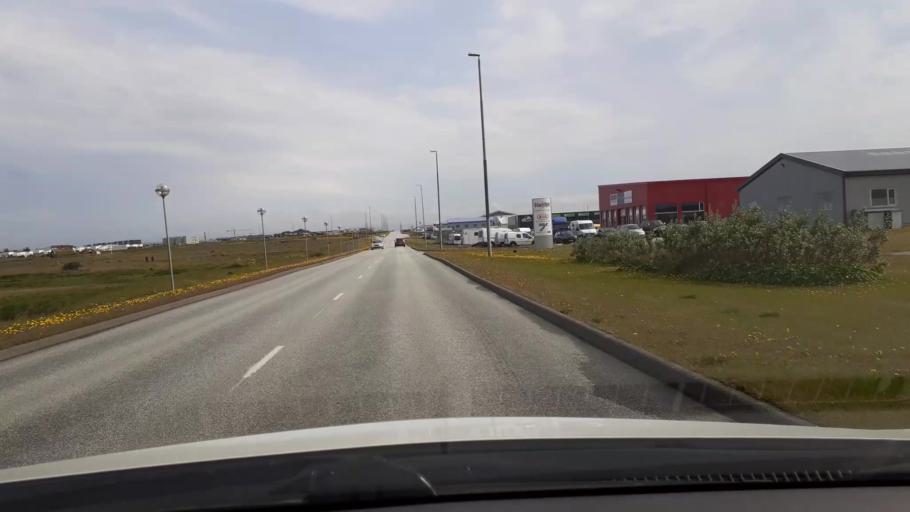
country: IS
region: Southern Peninsula
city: Reykjanesbaer
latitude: 63.9726
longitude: -22.5367
